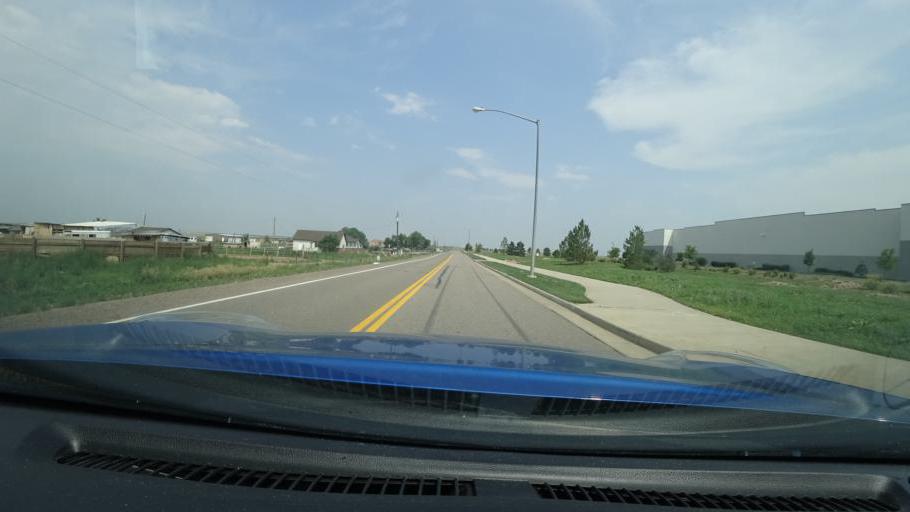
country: US
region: Colorado
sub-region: Adams County
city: Aurora
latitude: 39.7547
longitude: -104.7313
